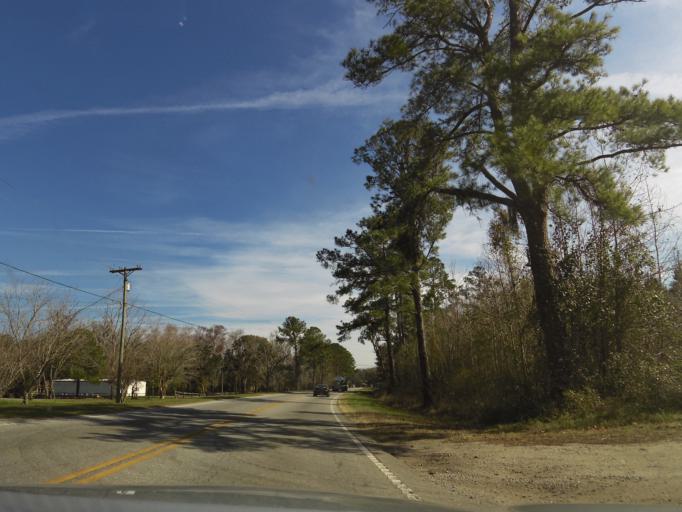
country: US
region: Georgia
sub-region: Glynn County
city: Dock Junction
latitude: 31.2738
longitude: -81.5674
